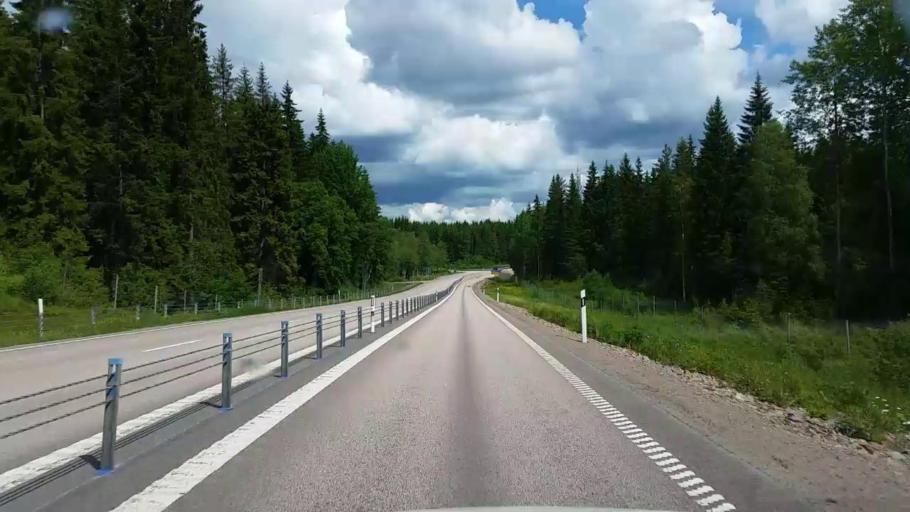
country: SE
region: Vaestmanland
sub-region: Norbergs Kommun
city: Norberg
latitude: 60.0898
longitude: 15.9882
